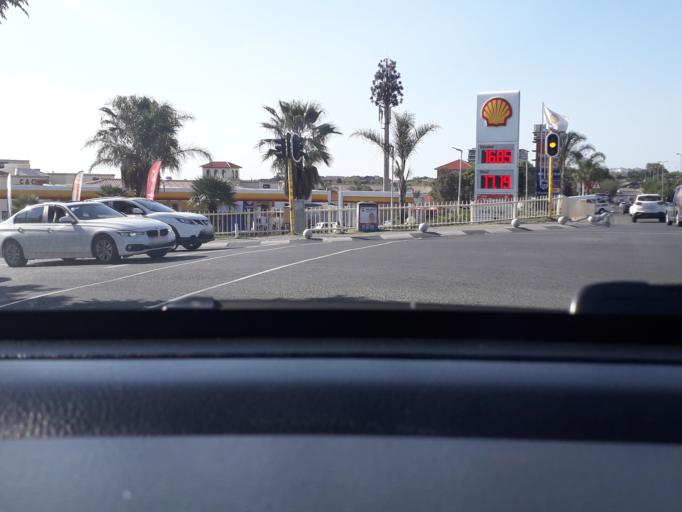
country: ZA
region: Gauteng
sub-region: City of Johannesburg Metropolitan Municipality
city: Midrand
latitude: -26.0381
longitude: 28.0805
